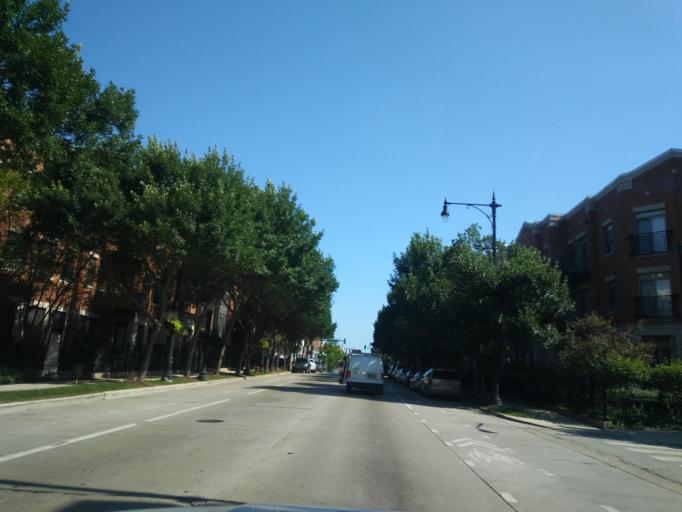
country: US
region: Illinois
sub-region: Cook County
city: Chicago
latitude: 41.8613
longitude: -87.6467
